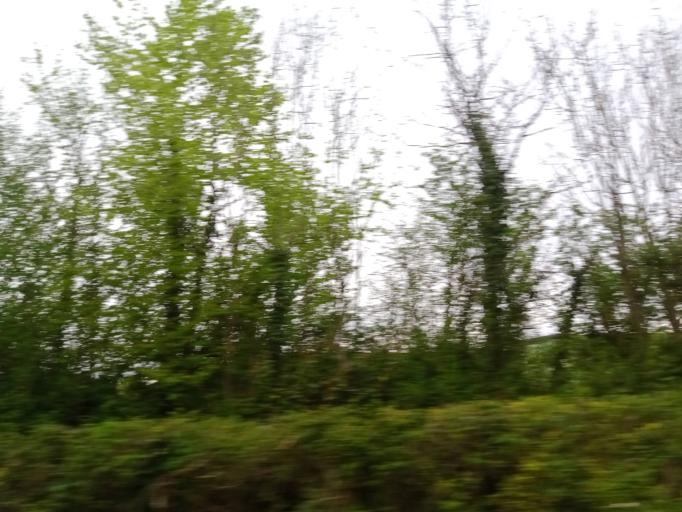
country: IE
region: Leinster
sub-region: Laois
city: Rathdowney
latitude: 52.7175
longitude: -7.4829
